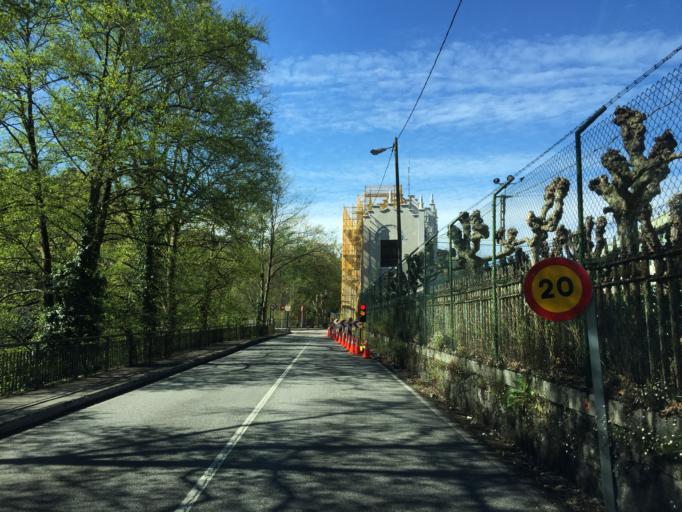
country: ES
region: Asturias
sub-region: Province of Asturias
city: Castandiello
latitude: 43.3459
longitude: -5.9719
